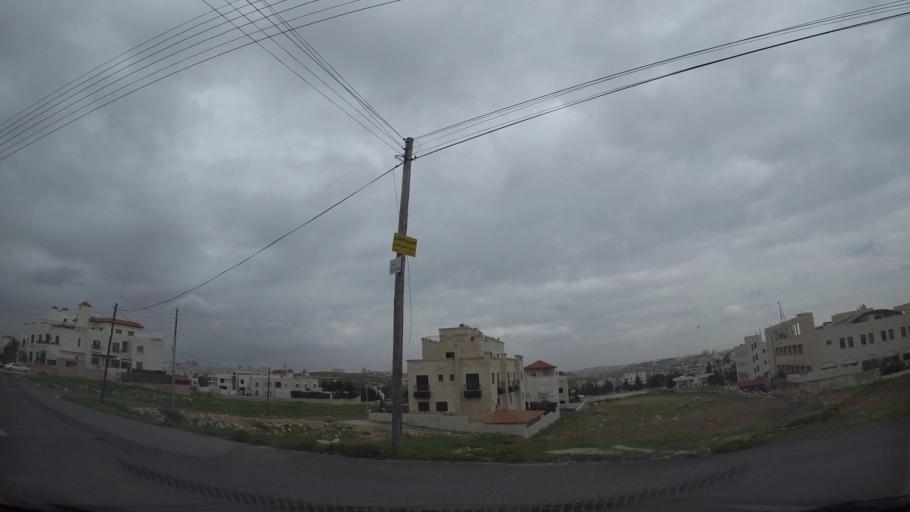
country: JO
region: Amman
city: Umm as Summaq
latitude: 31.9236
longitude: 35.8564
